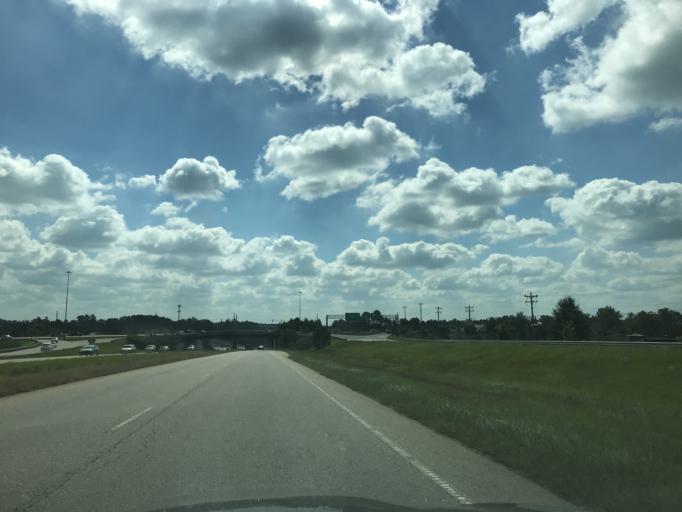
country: US
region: North Carolina
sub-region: Wake County
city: Wake Forest
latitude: 35.9684
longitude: -78.5416
